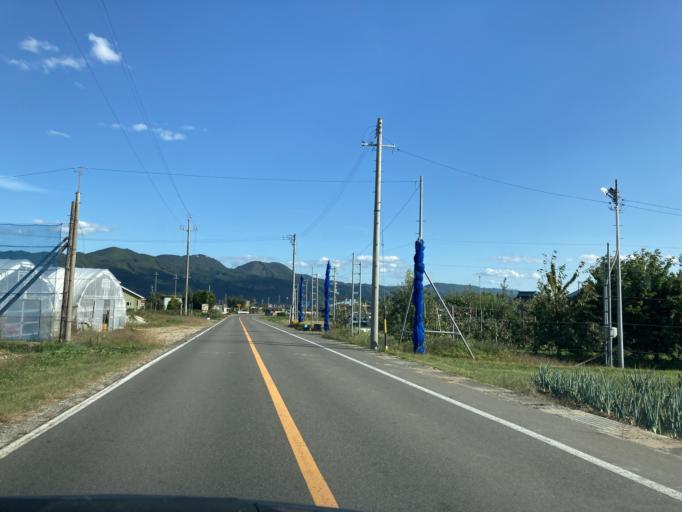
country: JP
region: Nagano
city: Omachi
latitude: 36.5259
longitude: 137.8299
